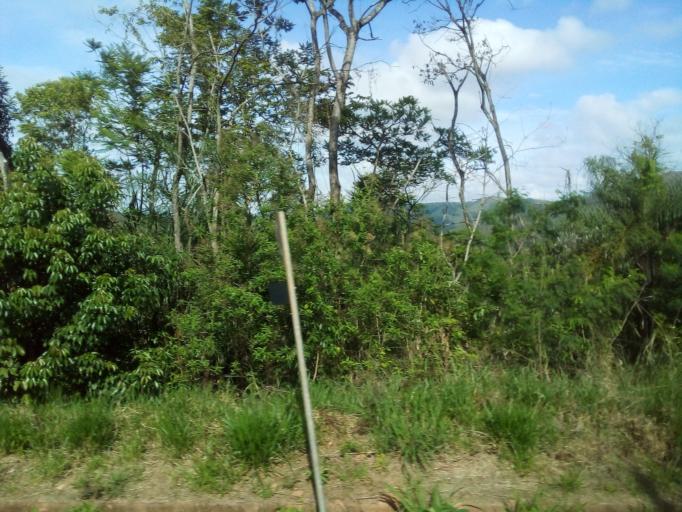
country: BR
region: Minas Gerais
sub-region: Caete
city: Caete
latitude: -19.8787
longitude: -43.7650
